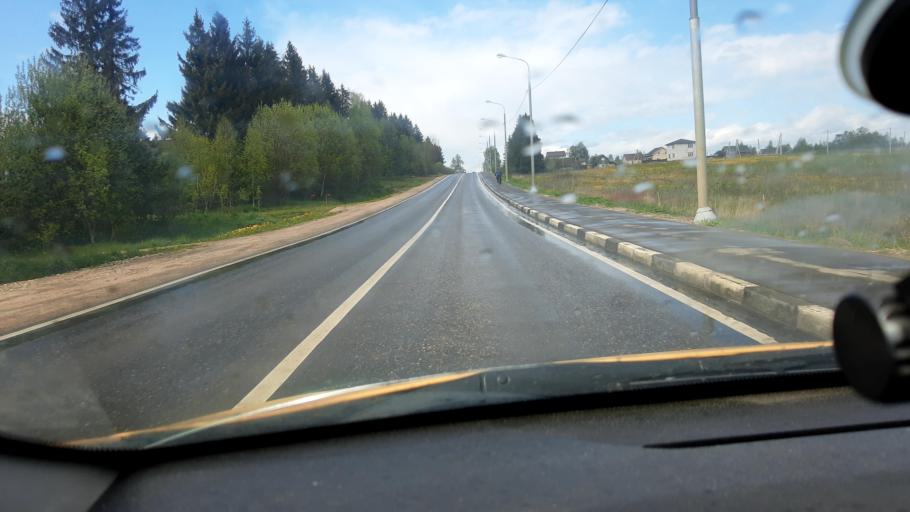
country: RU
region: Moskovskaya
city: Ruza
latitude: 55.7432
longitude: 36.1413
